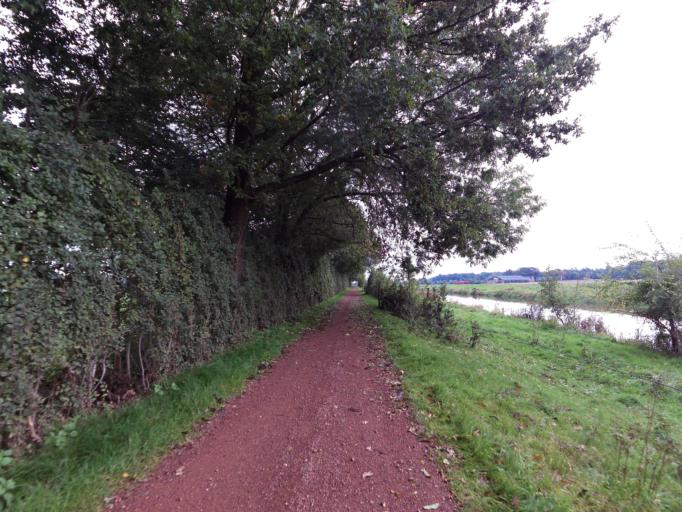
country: DE
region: North Rhine-Westphalia
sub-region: Regierungsbezirk Munster
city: Isselburg
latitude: 51.8470
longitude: 6.4916
